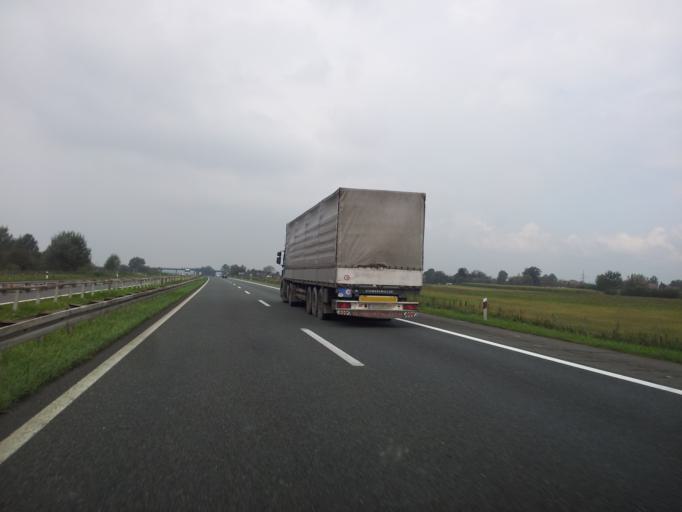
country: HR
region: Sisacko-Moslavacka
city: Repusnica
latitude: 45.4772
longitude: 16.7280
